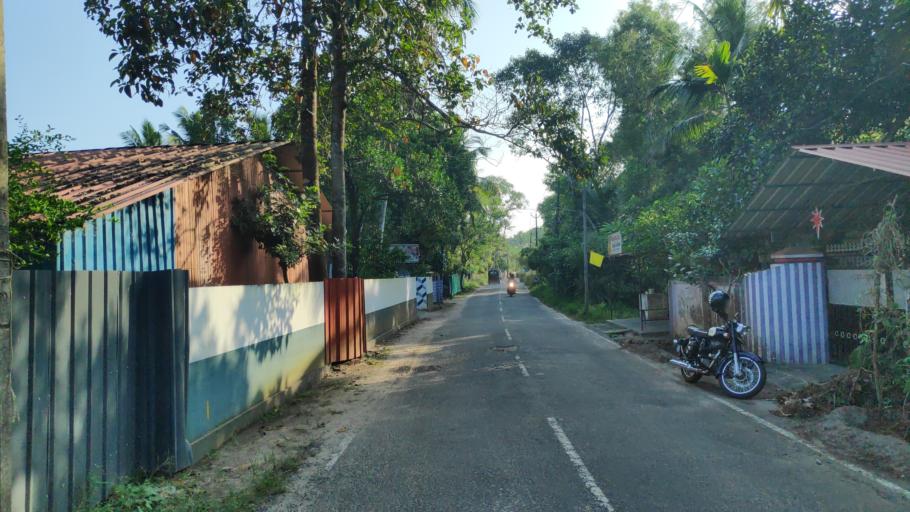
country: IN
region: Kerala
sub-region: Alappuzha
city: Alleppey
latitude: 9.5807
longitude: 76.3407
